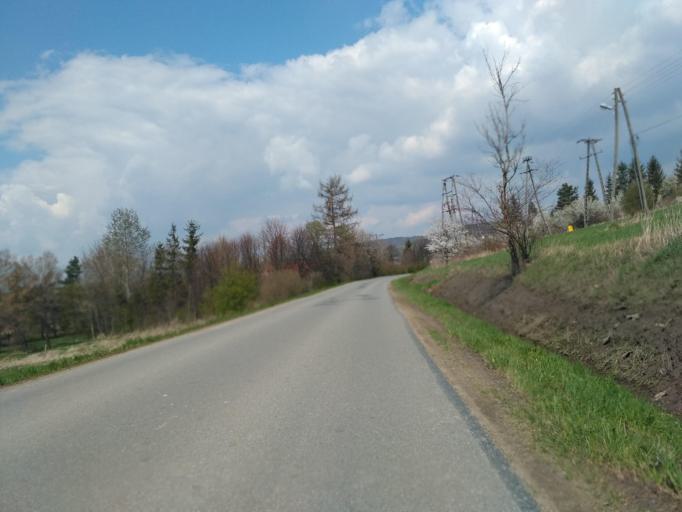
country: PL
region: Subcarpathian Voivodeship
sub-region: Powiat sanocki
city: Nowosielce-Gniewosz
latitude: 49.5464
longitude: 22.1081
